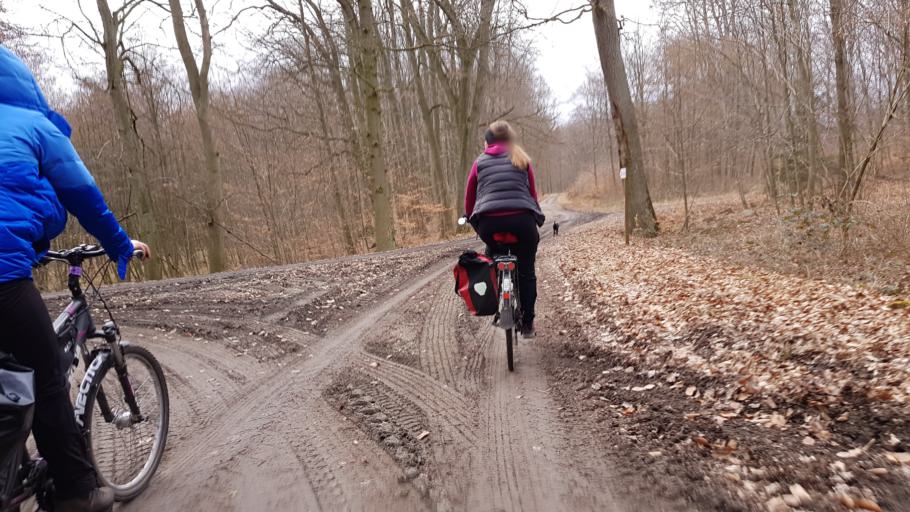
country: PL
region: West Pomeranian Voivodeship
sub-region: Powiat gryfinski
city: Banie
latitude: 53.0875
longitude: 14.7350
